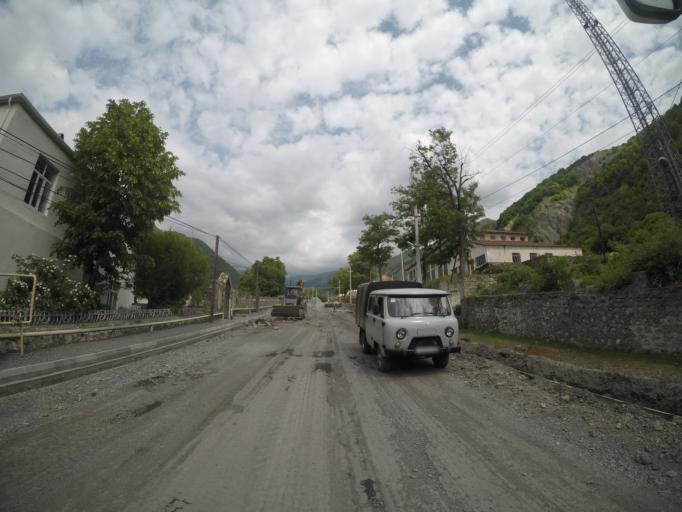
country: AZ
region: Qakh Rayon
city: Qaxbas
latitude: 41.4680
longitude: 47.0569
